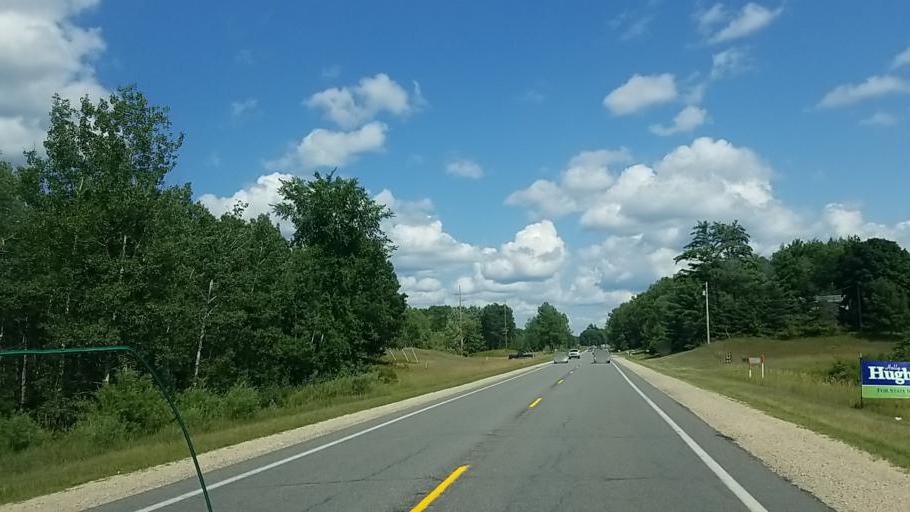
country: US
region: Michigan
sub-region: Newaygo County
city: Newaygo
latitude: 43.4055
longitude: -85.7829
